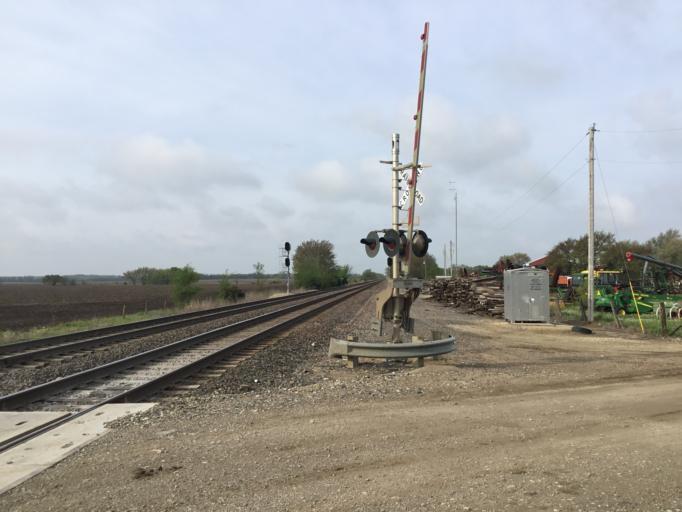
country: US
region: Kansas
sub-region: Butler County
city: Augusta
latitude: 37.7230
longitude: -96.9210
